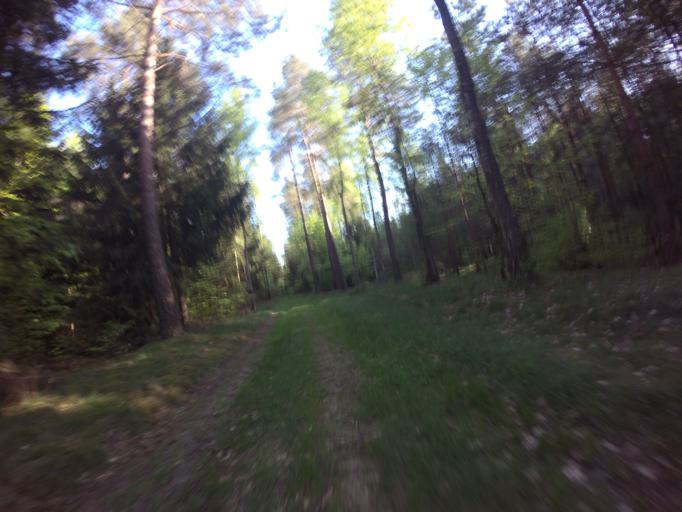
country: PL
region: West Pomeranian Voivodeship
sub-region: Powiat choszczenski
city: Drawno
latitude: 53.2205
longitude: 15.6825
